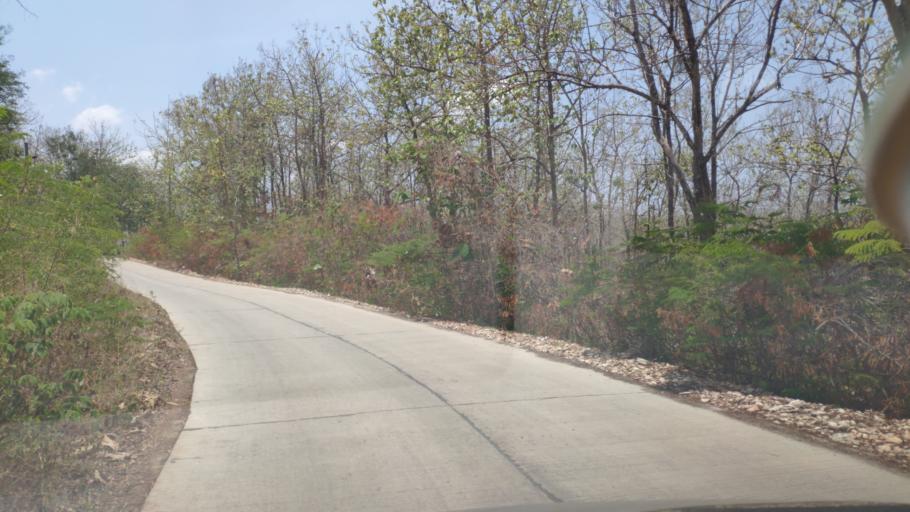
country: ID
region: Central Java
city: Randublatung
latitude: -7.2621
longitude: 111.3779
